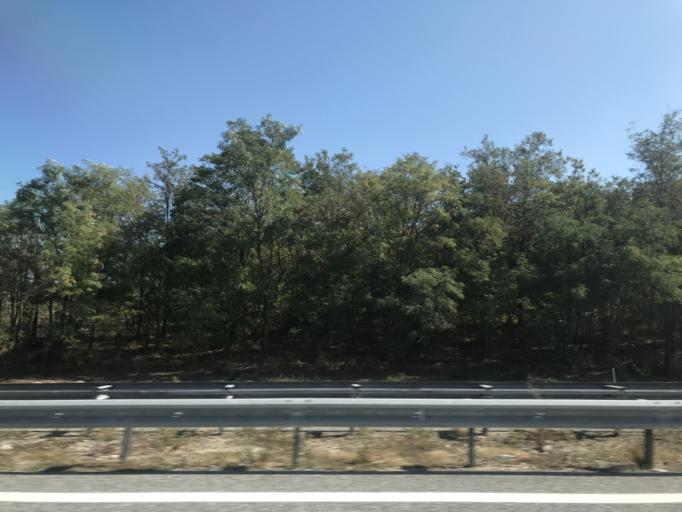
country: TR
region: Kirklareli
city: Luleburgaz
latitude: 41.4418
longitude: 27.3873
